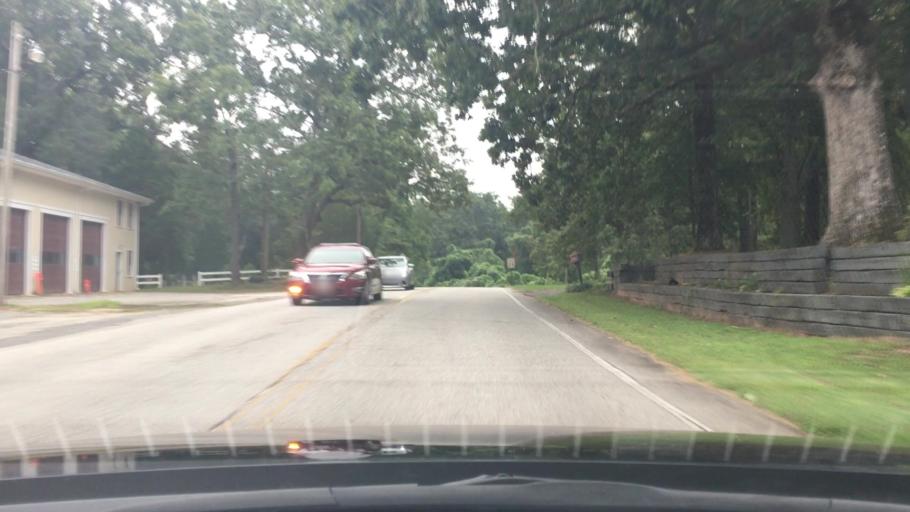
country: US
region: Georgia
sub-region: Coweta County
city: Senoia
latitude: 33.2901
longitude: -84.4583
